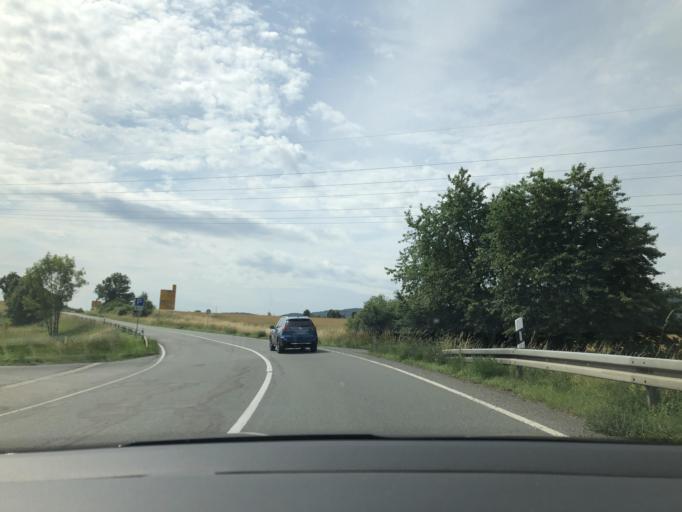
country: DE
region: Saxony-Anhalt
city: Blankenburg
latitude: 51.8151
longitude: 10.9400
